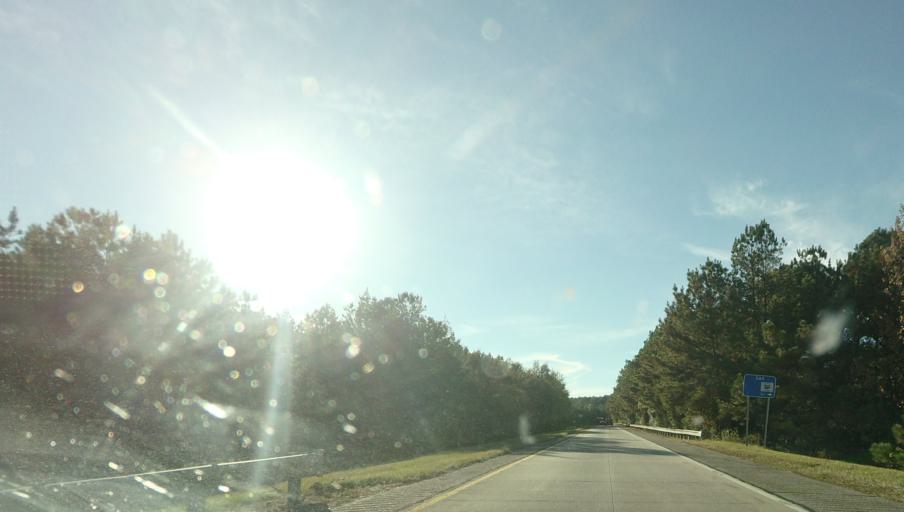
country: US
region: Georgia
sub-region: Muscogee County
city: Columbus
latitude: 32.5543
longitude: -84.9235
